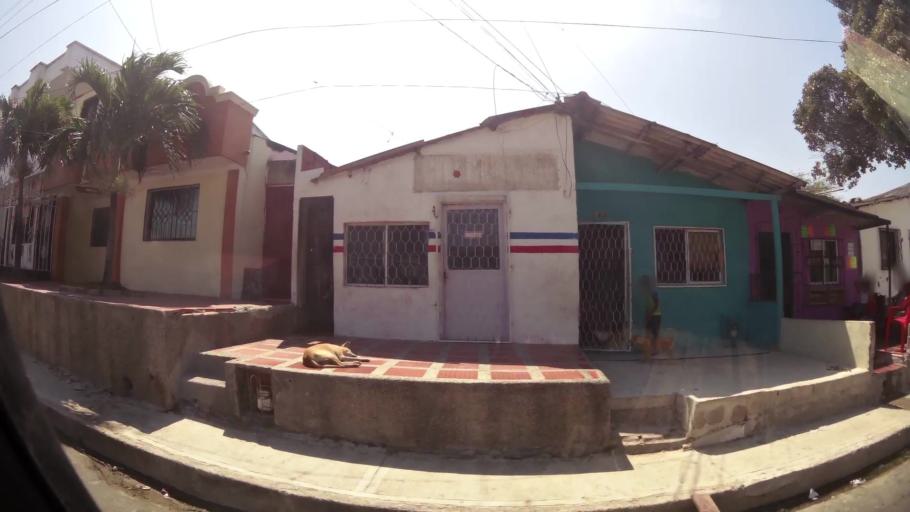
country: CO
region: Atlantico
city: Barranquilla
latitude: 10.9700
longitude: -74.8307
